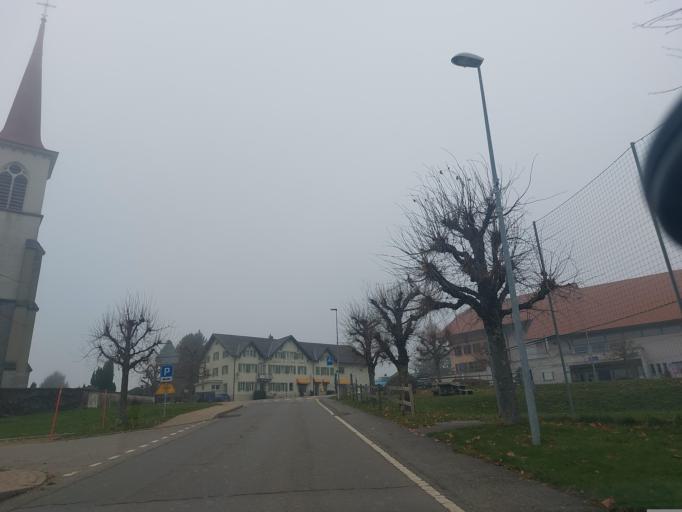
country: CH
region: Vaud
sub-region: Lavaux-Oron District
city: Oron-la-ville
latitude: 46.5762
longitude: 6.8701
